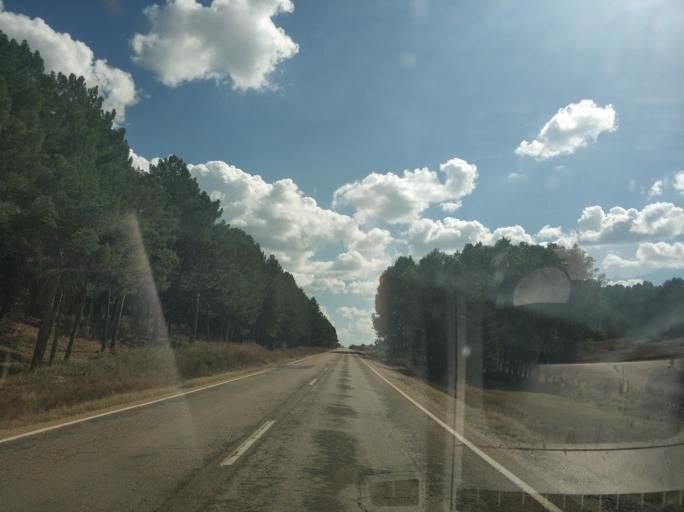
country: ES
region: Castille and Leon
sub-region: Provincia de Soria
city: San Leonardo de Yague
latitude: 41.8085
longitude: -3.0557
